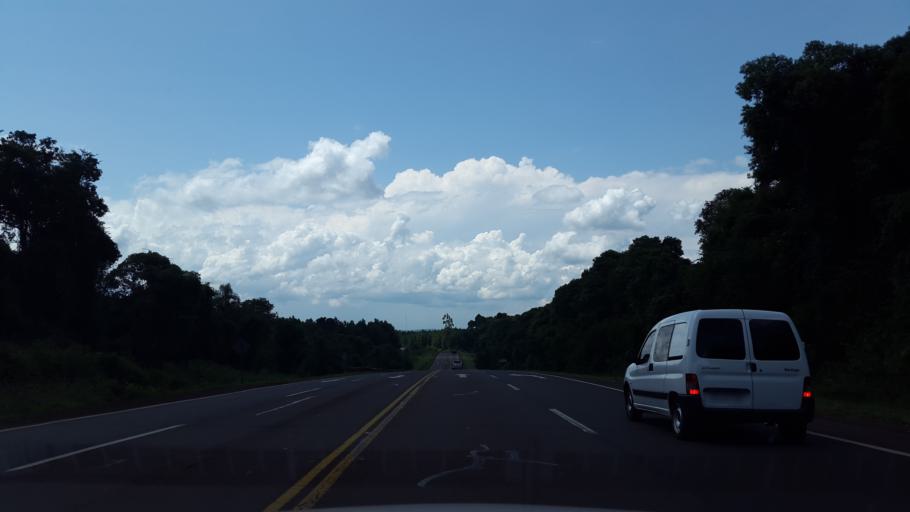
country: AR
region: Misiones
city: El Alcazar
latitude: -26.6972
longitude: -54.8351
